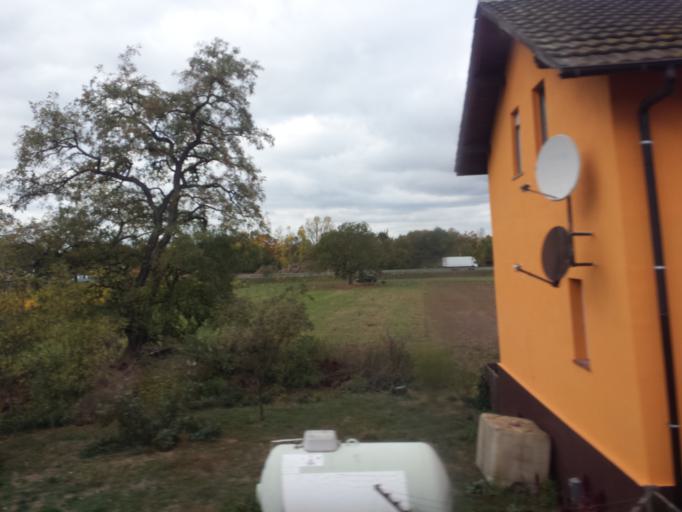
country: DE
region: Hesse
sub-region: Regierungsbezirk Darmstadt
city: Bickenbach
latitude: 49.7650
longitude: 8.6054
